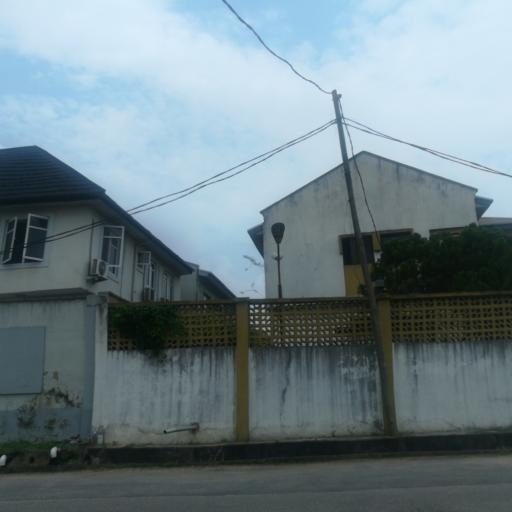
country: NG
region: Lagos
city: Ojota
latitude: 6.5759
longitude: 3.3810
